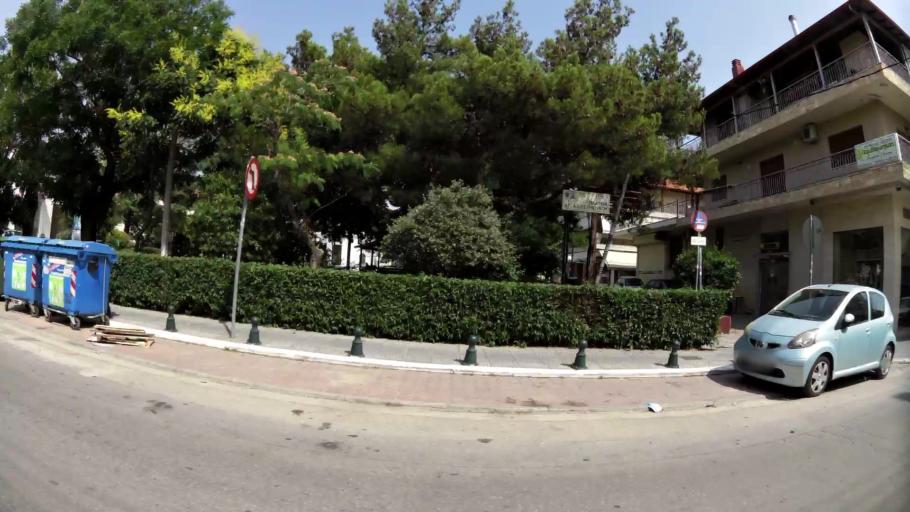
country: GR
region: Central Macedonia
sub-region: Nomos Thessalonikis
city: Efkarpia
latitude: 40.6884
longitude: 22.9545
